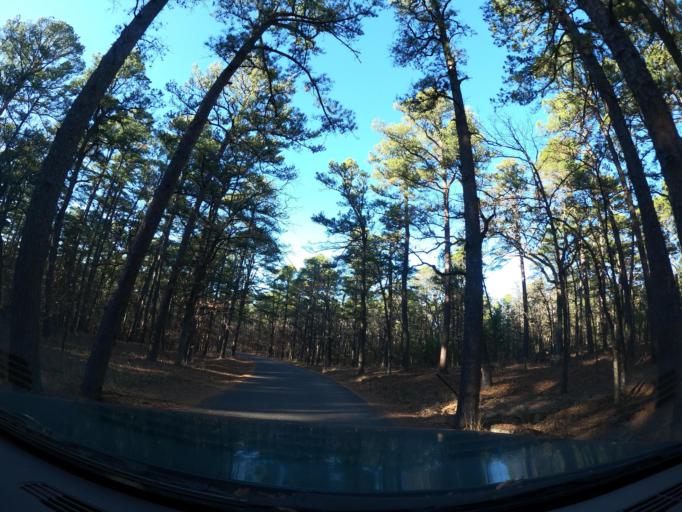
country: US
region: Oklahoma
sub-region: Latimer County
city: Wilburton
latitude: 34.9811
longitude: -95.3521
